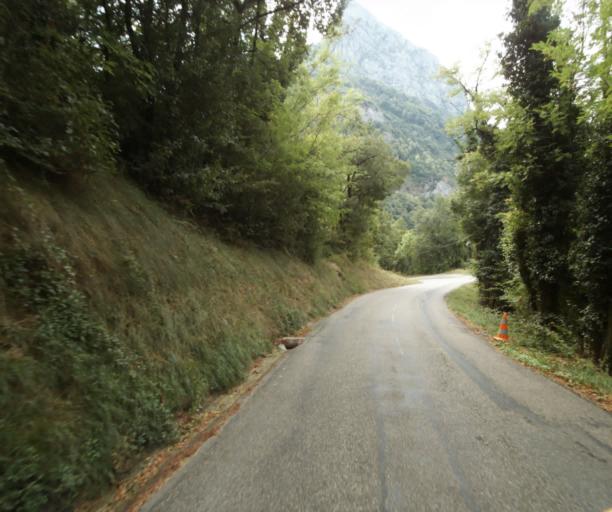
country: FR
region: Rhone-Alpes
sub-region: Departement de l'Isere
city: Saint-Egreve
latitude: 45.2518
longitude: 5.7014
